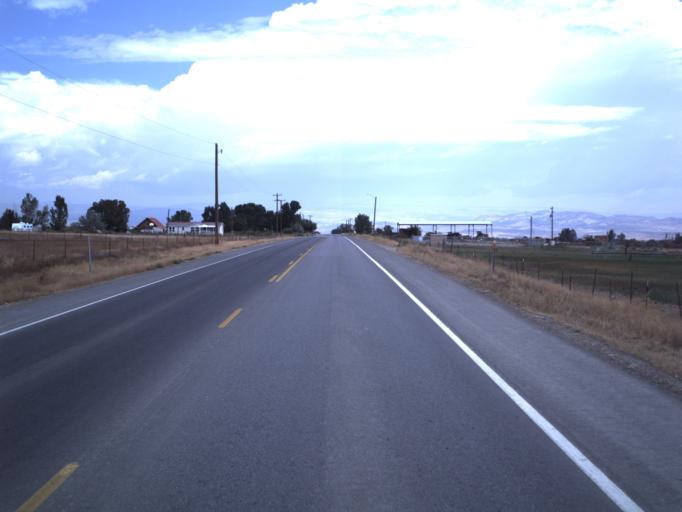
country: US
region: Utah
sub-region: Uintah County
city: Naples
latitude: 40.3807
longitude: -109.4985
